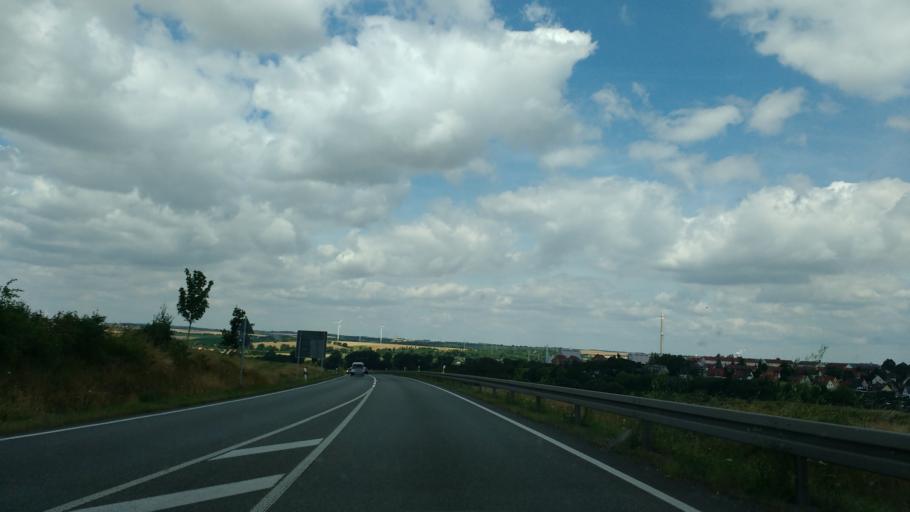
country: DE
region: Saxony-Anhalt
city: Zeitz
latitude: 51.0339
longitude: 12.1223
